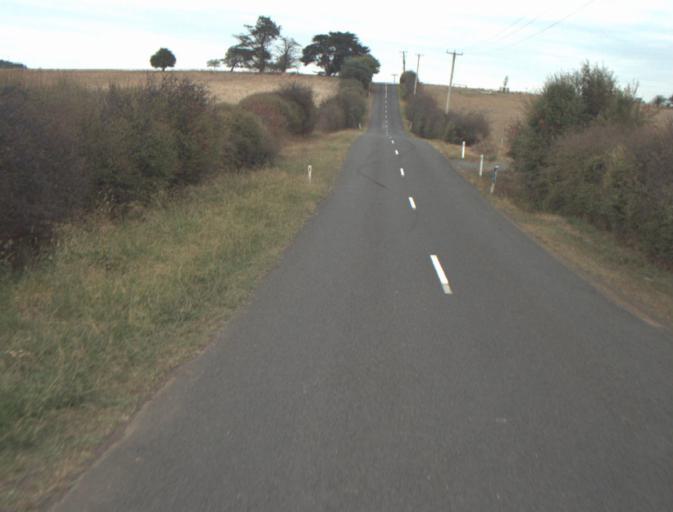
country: AU
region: Tasmania
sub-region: Northern Midlands
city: Evandale
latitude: -41.5176
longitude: 147.2173
